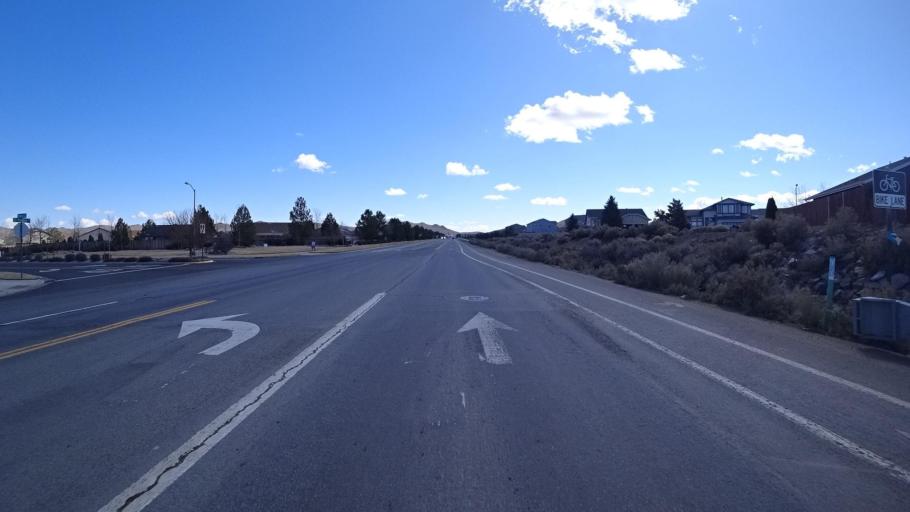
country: US
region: Nevada
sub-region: Washoe County
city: Lemmon Valley
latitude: 39.6424
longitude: -119.8629
